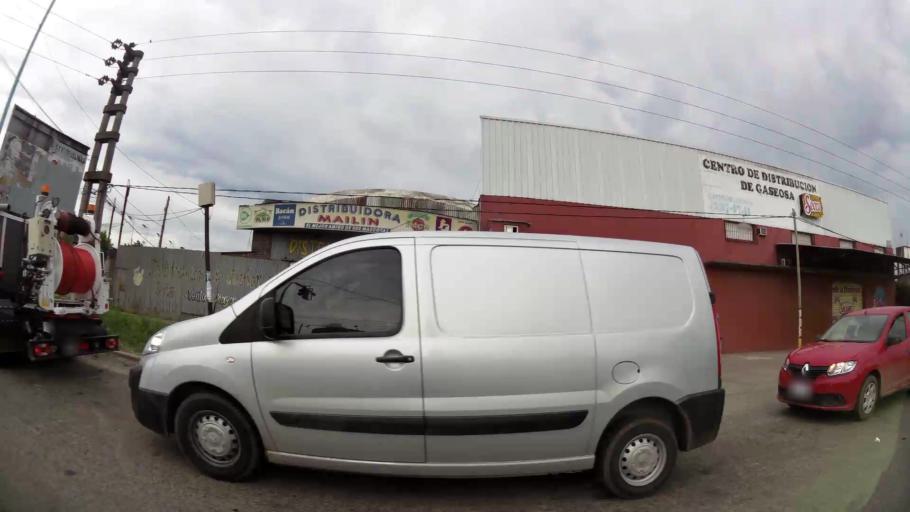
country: AR
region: Buenos Aires
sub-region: Partido de Quilmes
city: Quilmes
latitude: -34.7802
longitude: -58.2795
